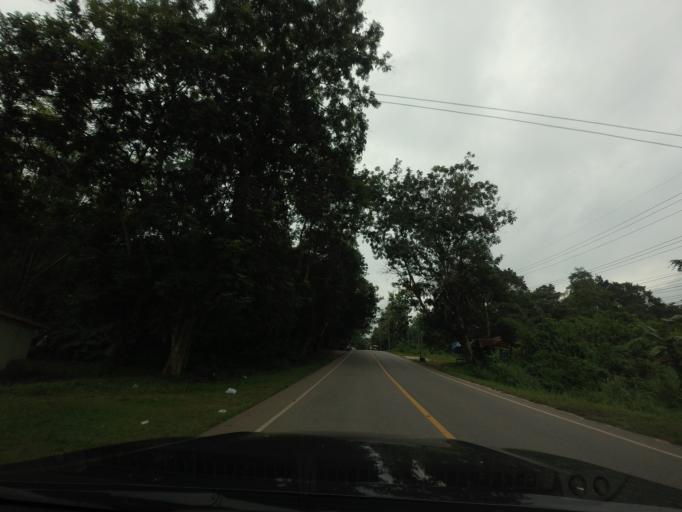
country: TH
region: Nong Khai
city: Si Chiang Mai
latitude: 17.9610
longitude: 102.5150
